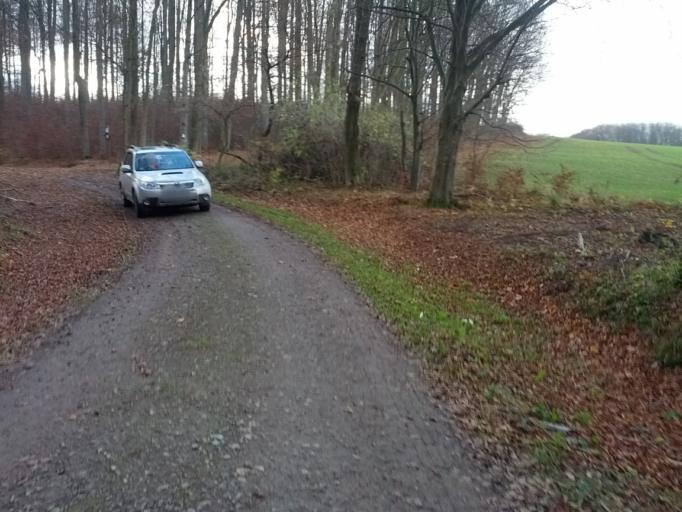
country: DE
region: Thuringia
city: Wolfsburg-Unkeroda
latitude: 50.9700
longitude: 10.2379
